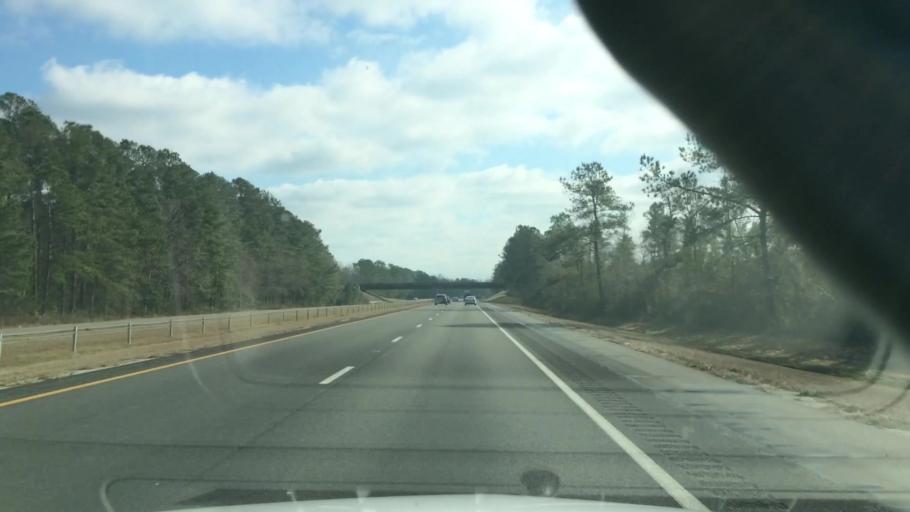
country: US
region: North Carolina
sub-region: Pender County
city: Burgaw
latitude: 34.6145
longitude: -77.9232
